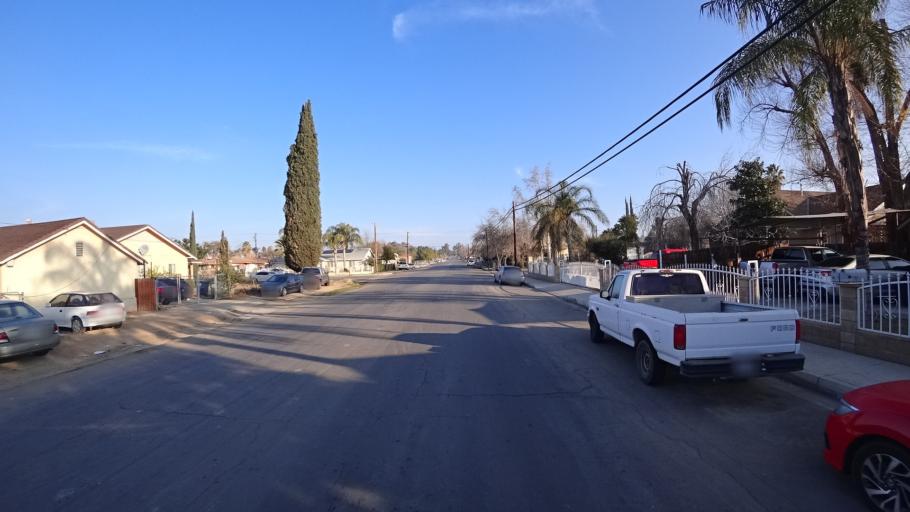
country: US
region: California
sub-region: Kern County
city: Bakersfield
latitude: 35.3833
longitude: -118.9839
